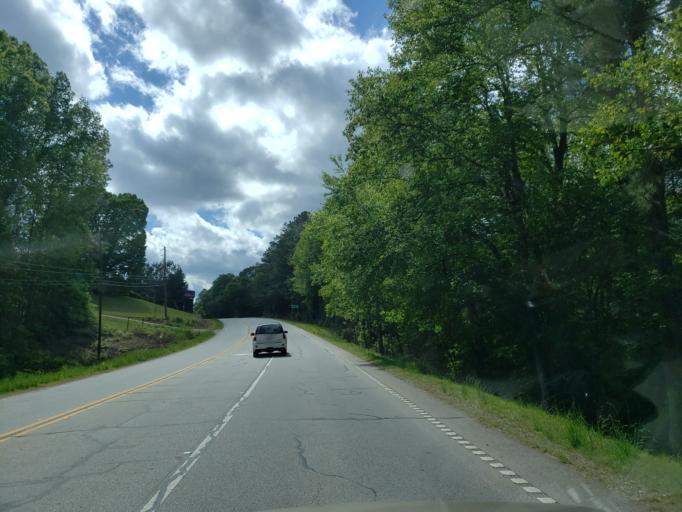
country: US
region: Georgia
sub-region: Haralson County
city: Bremen
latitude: 33.7052
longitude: -85.1799
